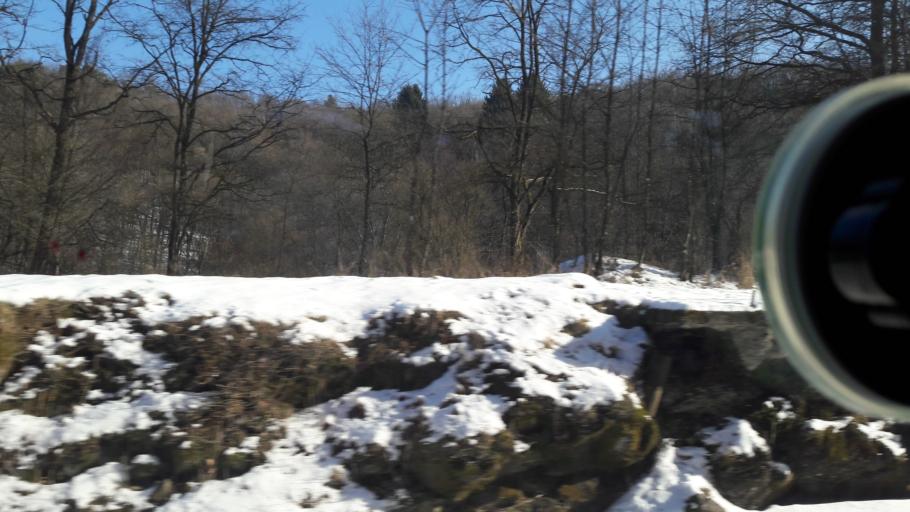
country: DE
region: Saarland
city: Namborn
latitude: 49.5373
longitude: 7.1441
